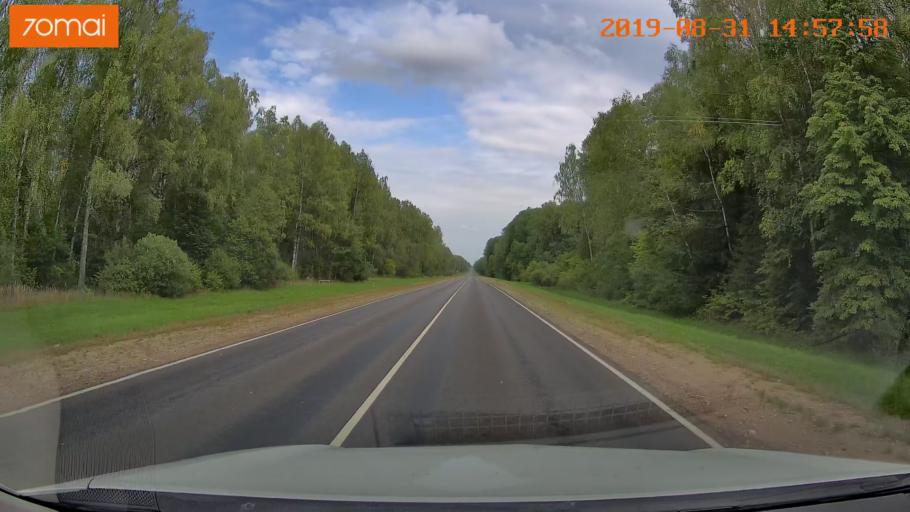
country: RU
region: Kaluga
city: Spas-Demensk
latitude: 54.3142
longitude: 33.9702
